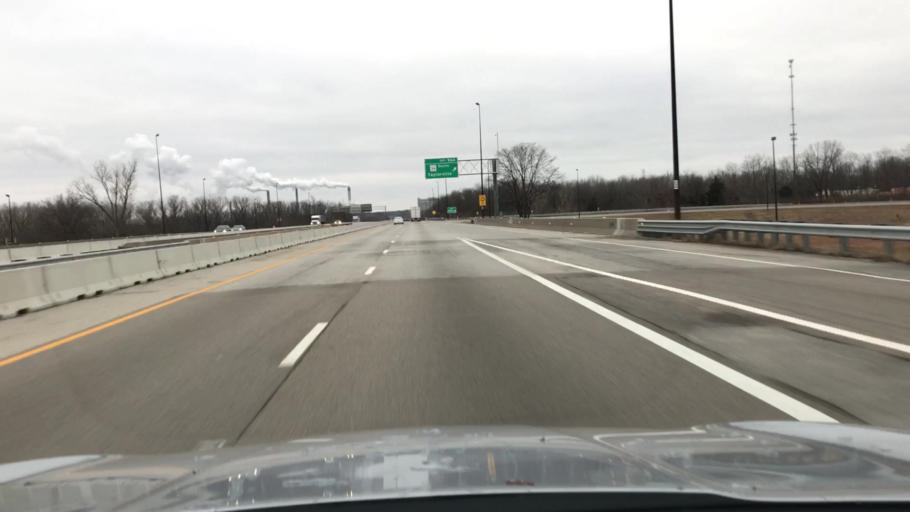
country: US
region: Illinois
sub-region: Sangamon County
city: Grandview
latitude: 39.7870
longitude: -89.5994
